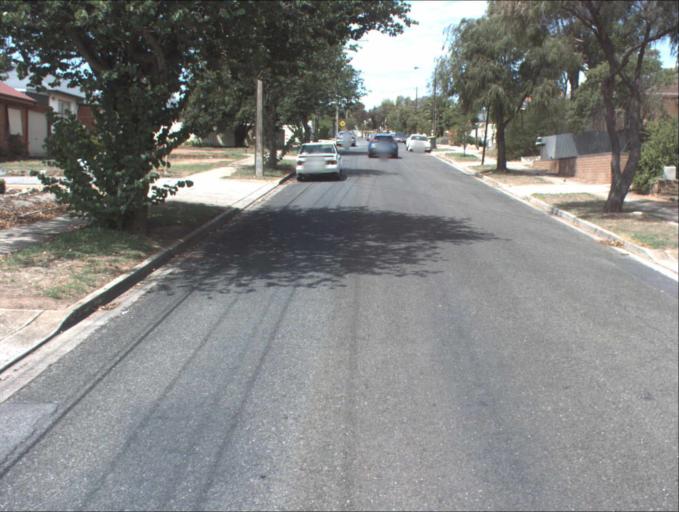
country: AU
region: South Australia
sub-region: Port Adelaide Enfield
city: Enfield
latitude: -34.8509
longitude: 138.6067
